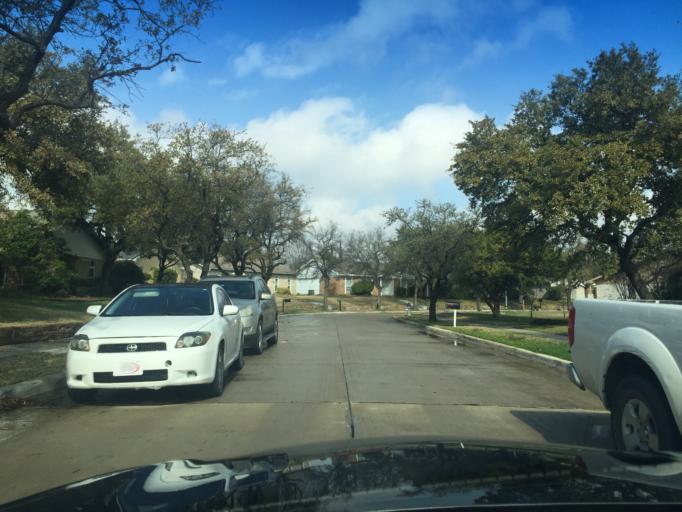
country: US
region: Texas
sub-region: Dallas County
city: Carrollton
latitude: 32.9948
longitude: -96.8782
